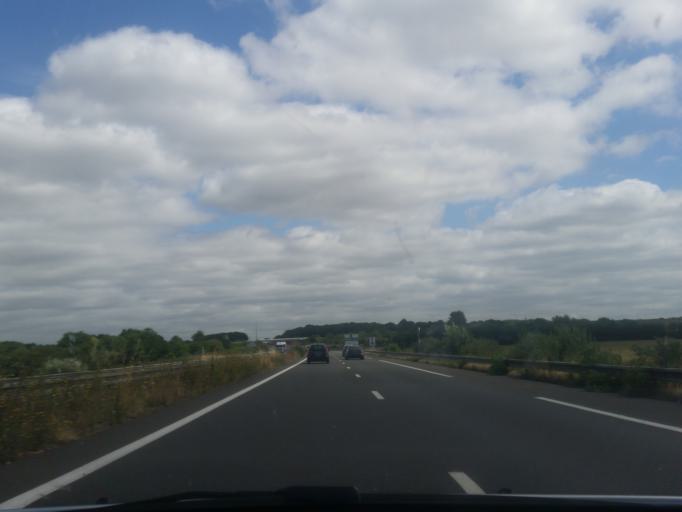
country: FR
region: Pays de la Loire
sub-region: Departement de Maine-et-Loire
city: Saint-Leger-des-Bois
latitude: 47.4536
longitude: -0.7085
